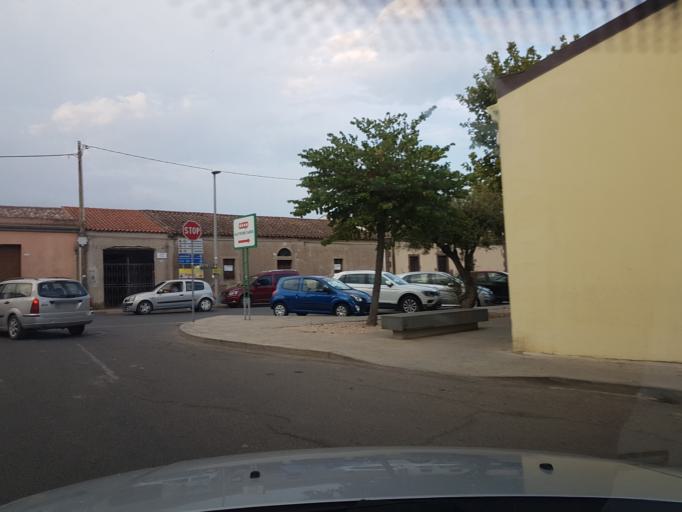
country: IT
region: Sardinia
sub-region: Provincia di Oristano
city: Cabras
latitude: 39.9272
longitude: 8.5332
